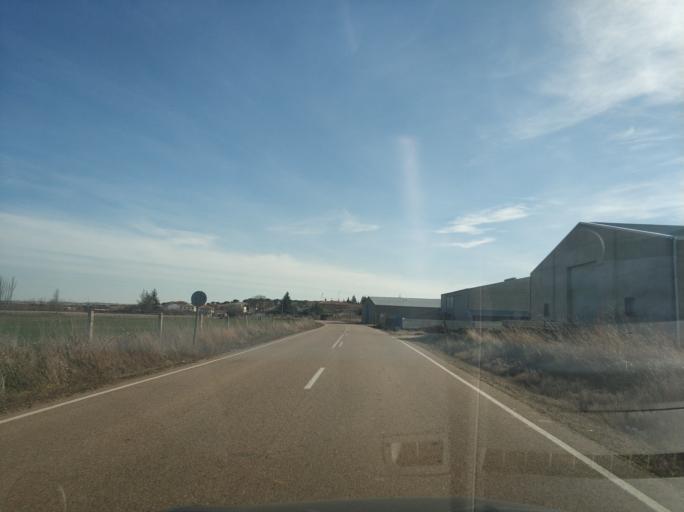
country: ES
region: Castille and Leon
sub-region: Provincia de Salamanca
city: Florida de Liebana
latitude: 41.0294
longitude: -5.7639
